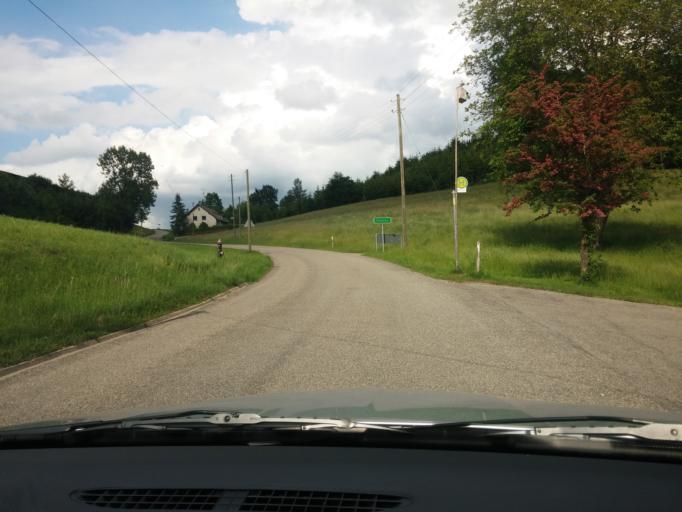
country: DE
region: Bavaria
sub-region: Swabia
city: Woringen
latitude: 47.8831
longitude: 10.1885
